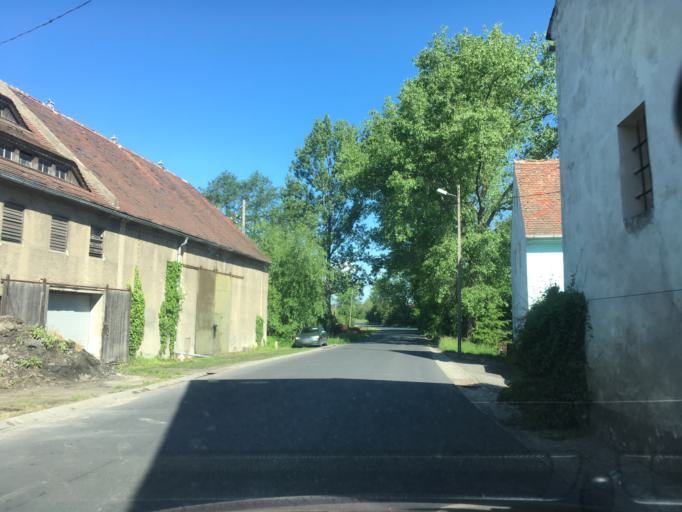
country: PL
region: Lower Silesian Voivodeship
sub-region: Powiat zgorzelecki
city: Sulikow
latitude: 51.0918
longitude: 15.0496
